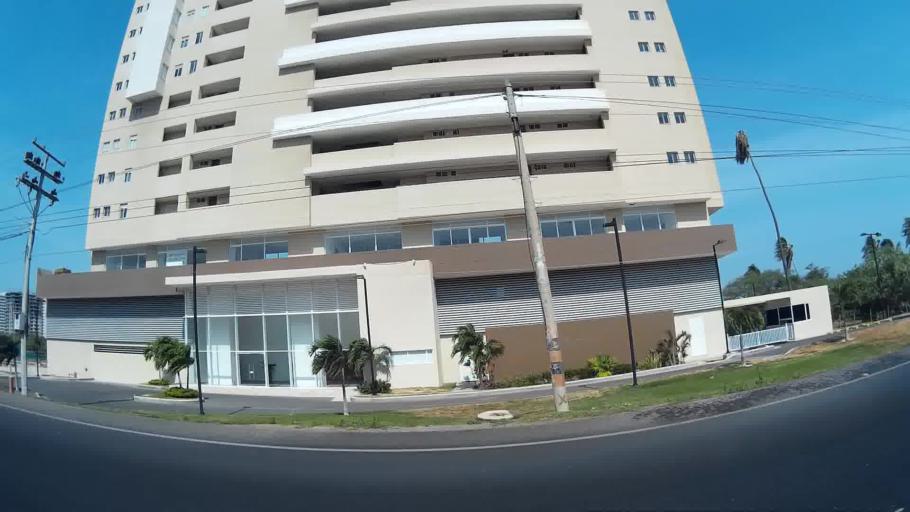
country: CO
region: Magdalena
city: Santa Marta
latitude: 11.1553
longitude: -74.2230
